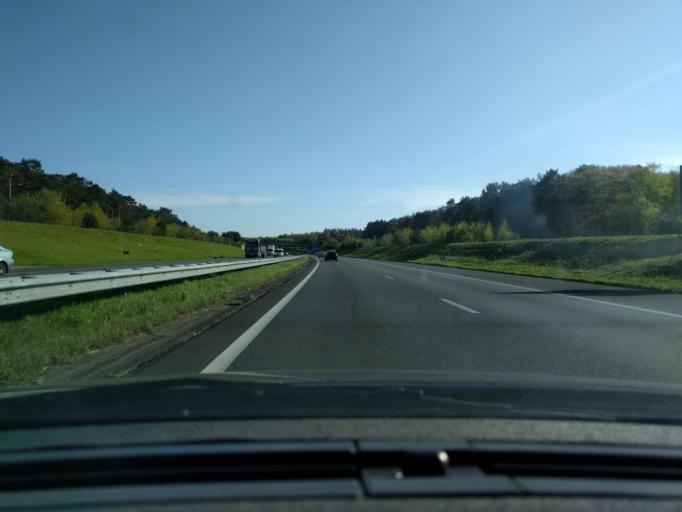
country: NL
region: North Brabant
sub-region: Gemeente Son en Breugel
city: Son
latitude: 51.5248
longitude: 5.4691
